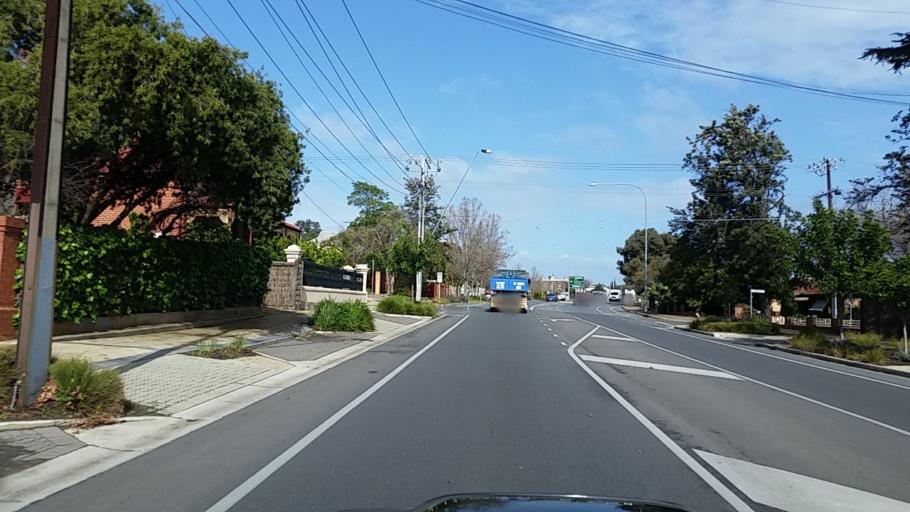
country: AU
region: South Australia
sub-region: Adelaide
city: North Adelaide
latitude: -34.8947
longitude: 138.5855
